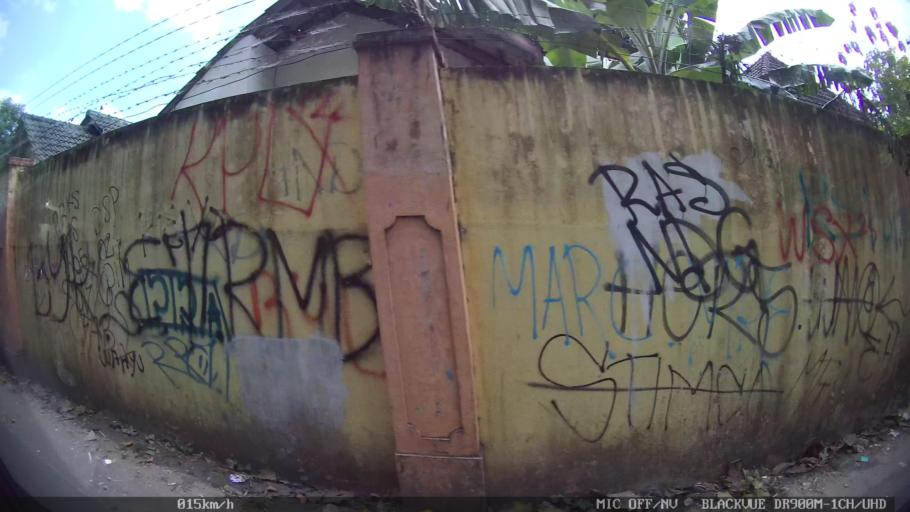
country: ID
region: Daerah Istimewa Yogyakarta
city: Gamping Lor
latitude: -7.8087
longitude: 110.3442
